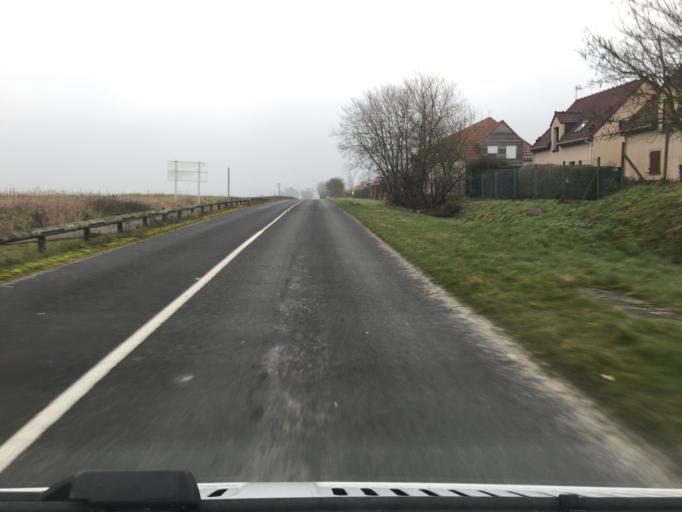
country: FR
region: Picardie
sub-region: Departement de la Somme
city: Le Crotoy
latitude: 50.2283
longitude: 1.6155
